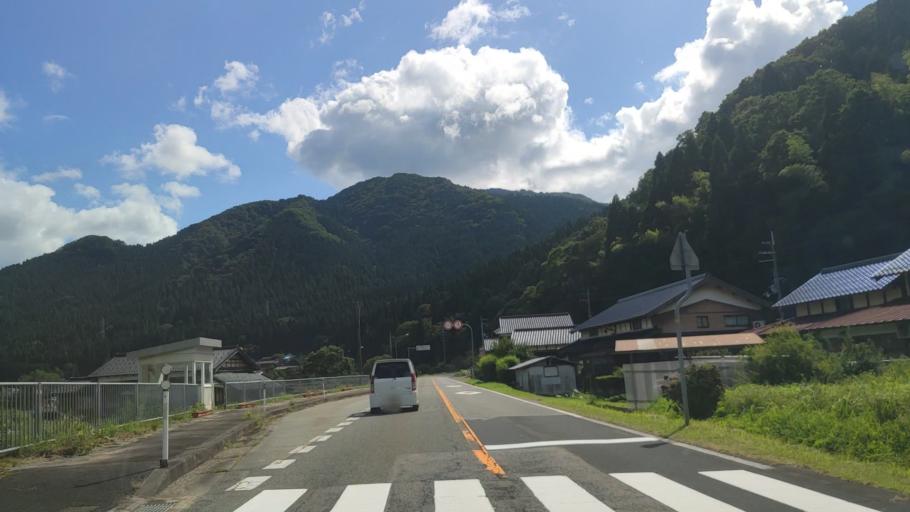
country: JP
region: Hyogo
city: Toyooka
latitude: 35.4951
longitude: 134.9805
